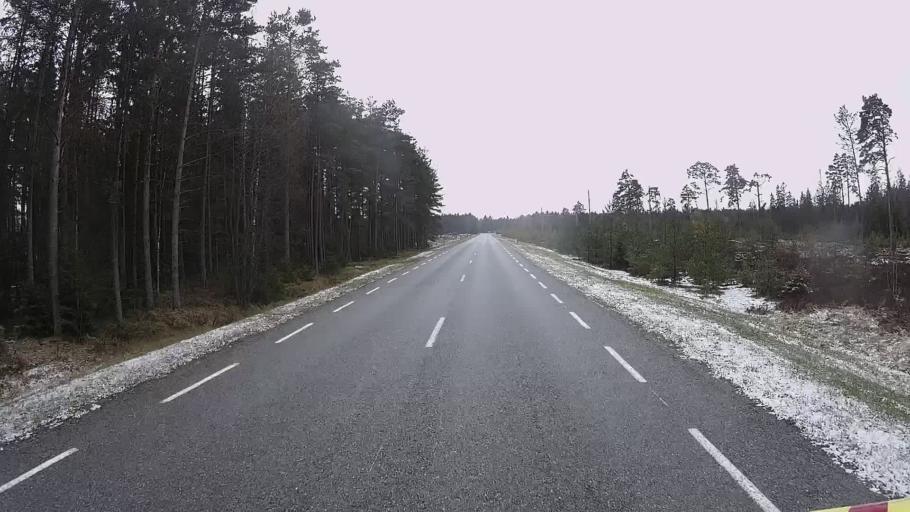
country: EE
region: Hiiumaa
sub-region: Kaerdla linn
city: Kardla
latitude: 59.0172
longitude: 22.6718
